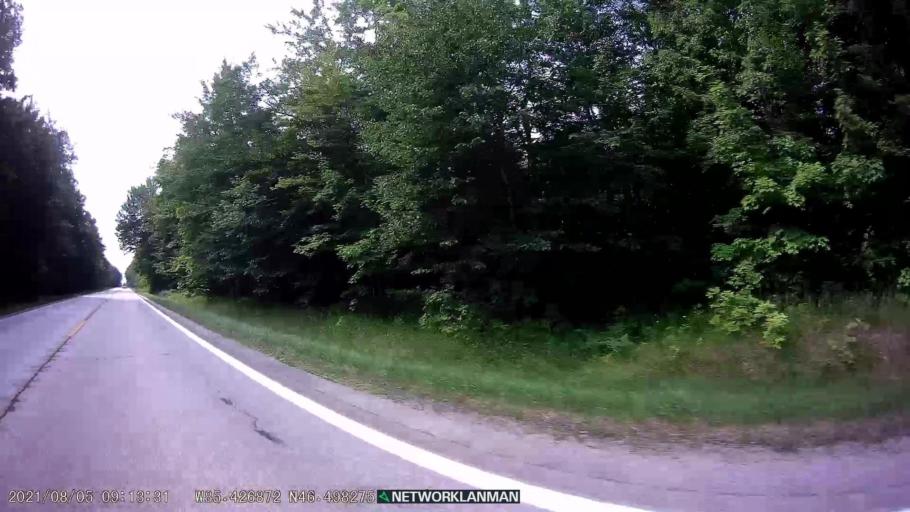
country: US
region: Michigan
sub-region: Luce County
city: Newberry
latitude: 46.4979
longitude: -85.4267
